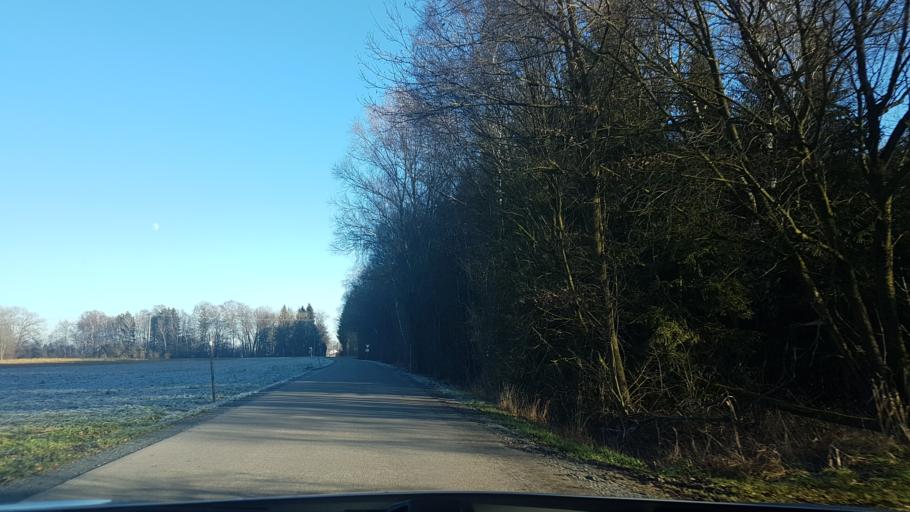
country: DE
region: Bavaria
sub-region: Upper Bavaria
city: Eichenried
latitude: 48.2805
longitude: 11.7761
